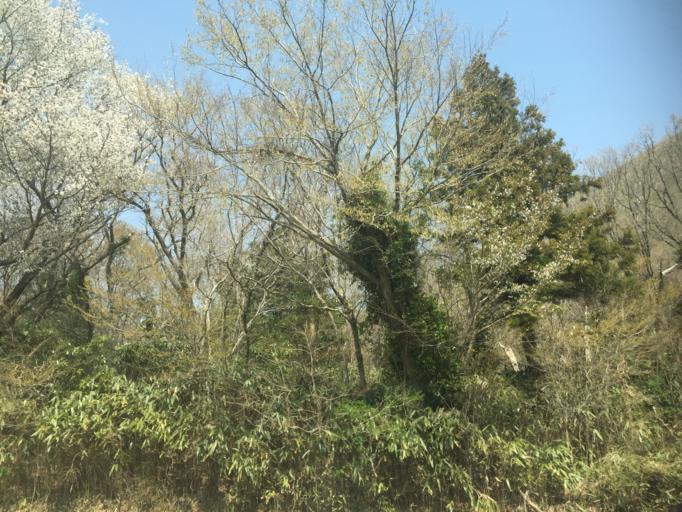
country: JP
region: Shizuoka
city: Ito
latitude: 34.9017
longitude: 139.0897
